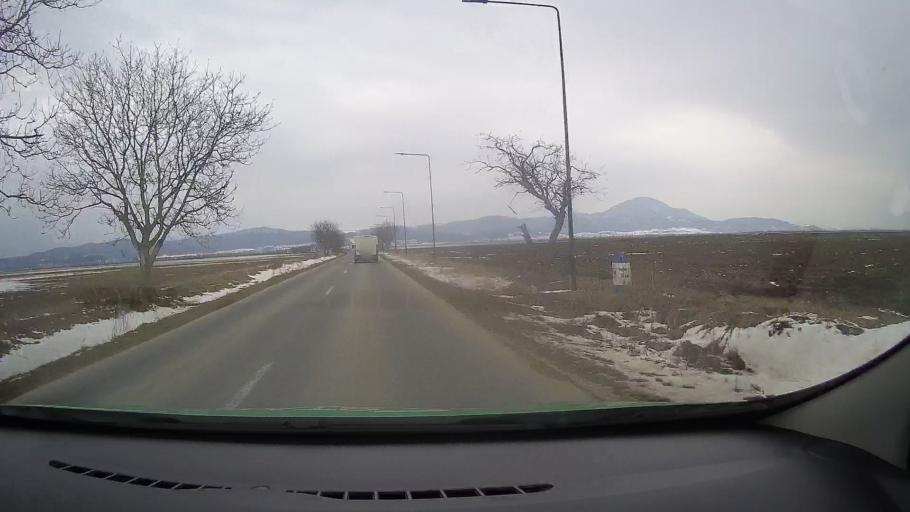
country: RO
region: Brasov
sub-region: Comuna Cristian
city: Cristian
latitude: 45.6321
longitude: 25.4596
